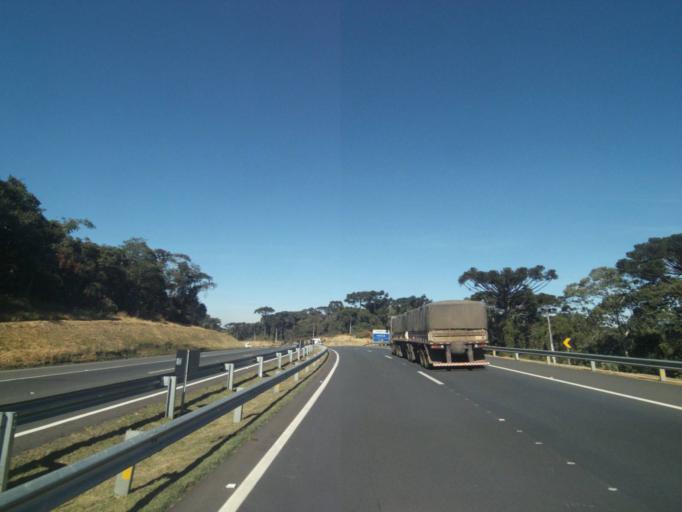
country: BR
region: Parana
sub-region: Carambei
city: Carambei
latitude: -24.9055
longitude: -50.4225
